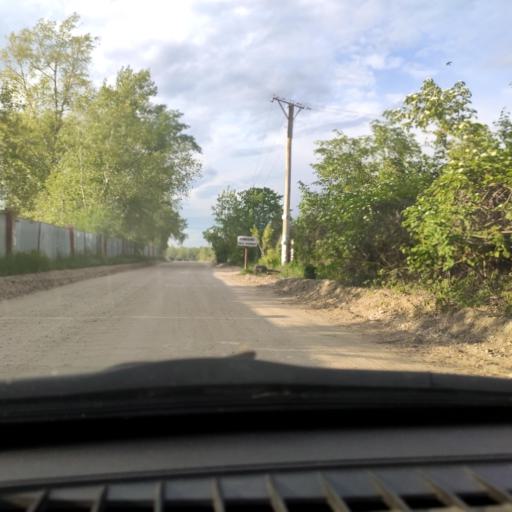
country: RU
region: Samara
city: Zhigulevsk
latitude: 53.4513
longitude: 49.5345
